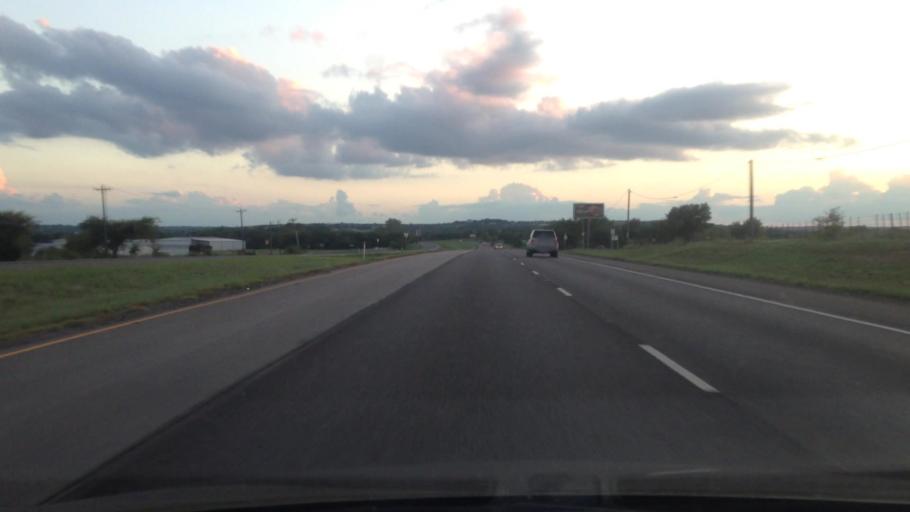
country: US
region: Texas
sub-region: Parker County
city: Aledo
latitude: 32.5900
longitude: -97.5885
